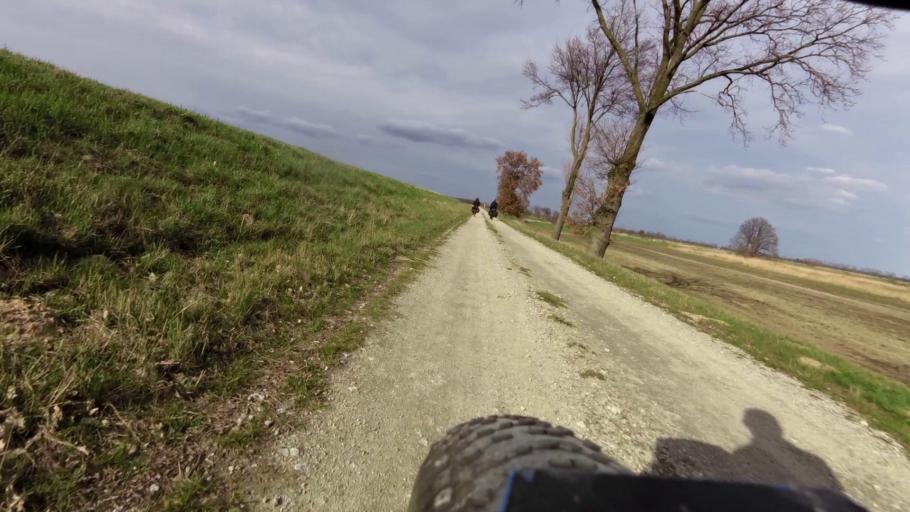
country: PL
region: Lubusz
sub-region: Powiat gorzowski
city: Kostrzyn nad Odra
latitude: 52.5508
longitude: 14.6212
